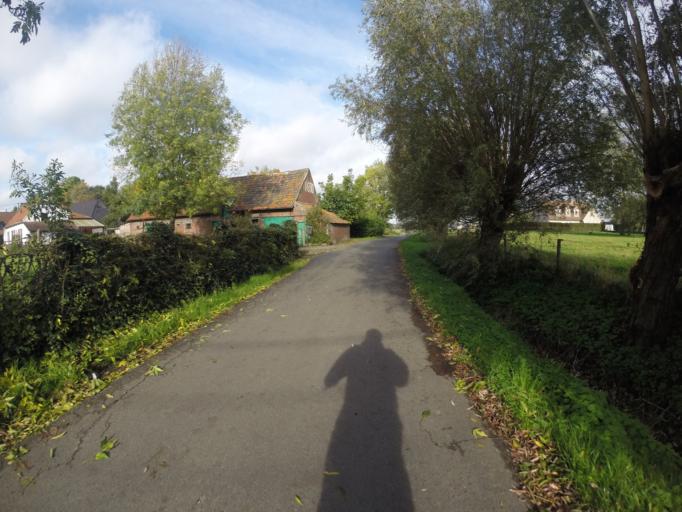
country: BE
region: Flanders
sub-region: Provincie Oost-Vlaanderen
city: Knesselare
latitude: 51.1164
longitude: 3.4175
